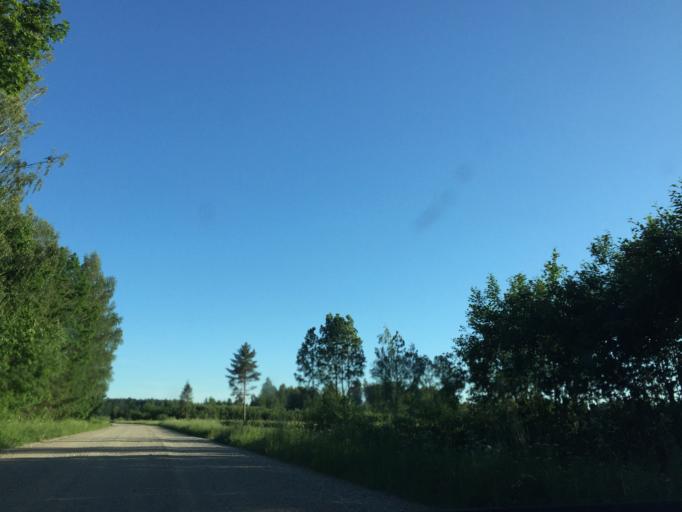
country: LV
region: Broceni
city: Broceni
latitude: 56.8511
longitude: 22.5645
